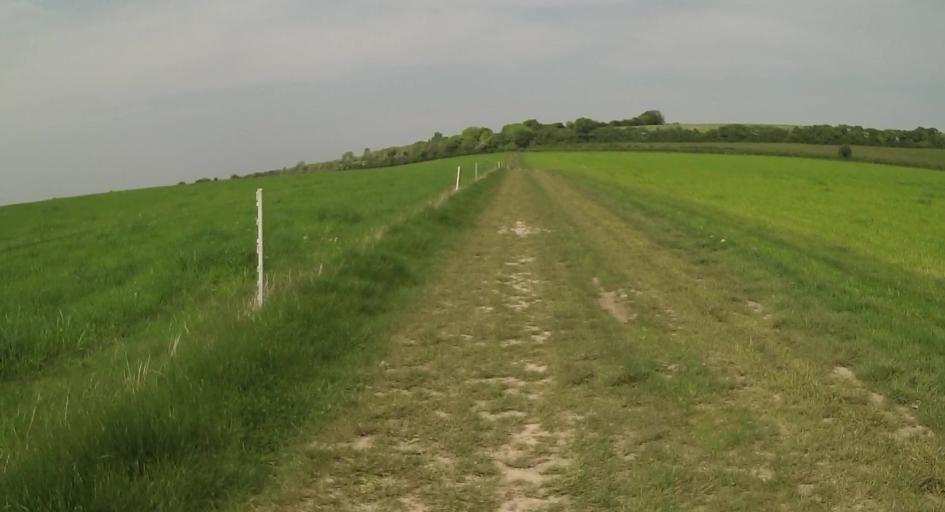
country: GB
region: England
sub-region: Hampshire
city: Kingsclere
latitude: 51.3153
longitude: -1.2329
